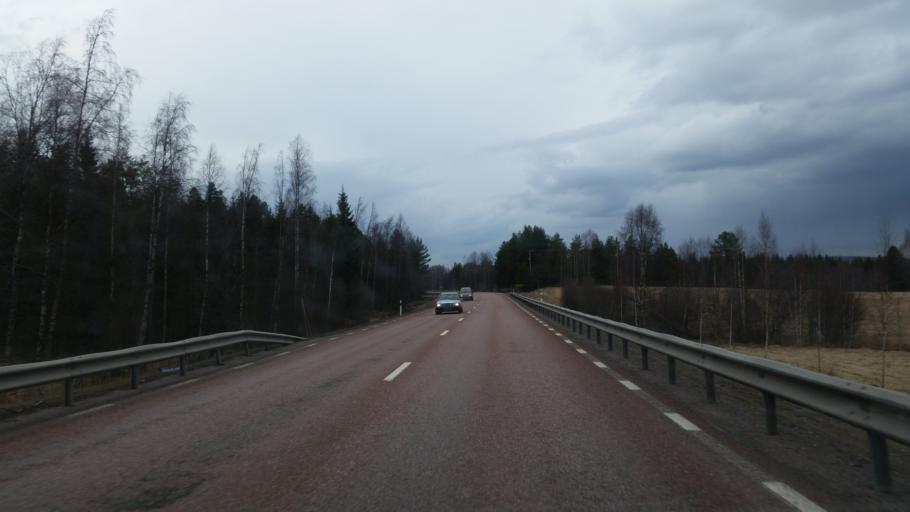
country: SE
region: Gaevleborg
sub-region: Ljusdals Kommun
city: Ljusdal
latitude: 61.8022
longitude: 16.1127
